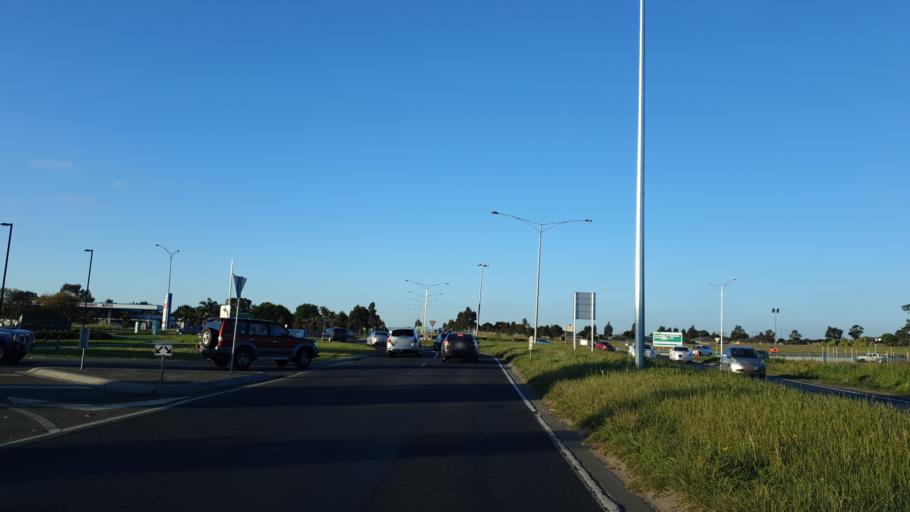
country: AU
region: Victoria
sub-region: Casey
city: Cranbourne North
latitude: -38.0857
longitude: 145.2952
